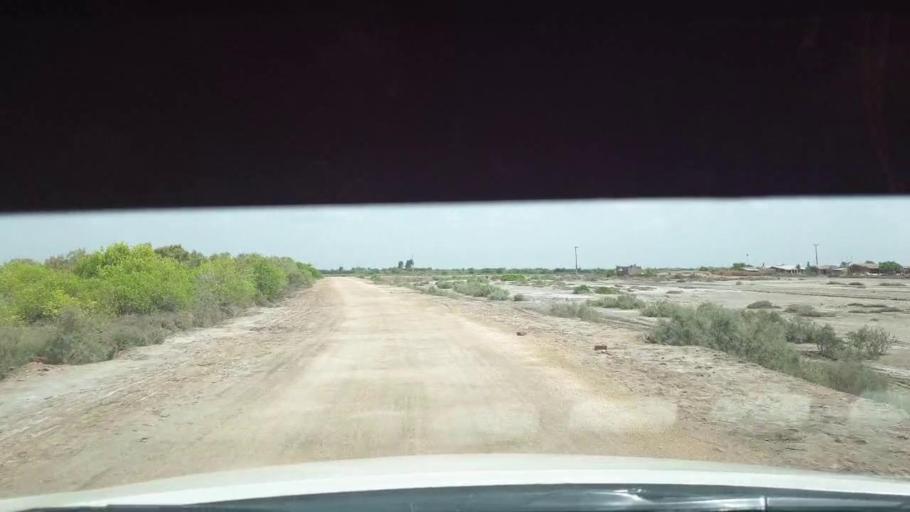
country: PK
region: Sindh
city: Kadhan
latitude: 24.5186
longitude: 68.9702
